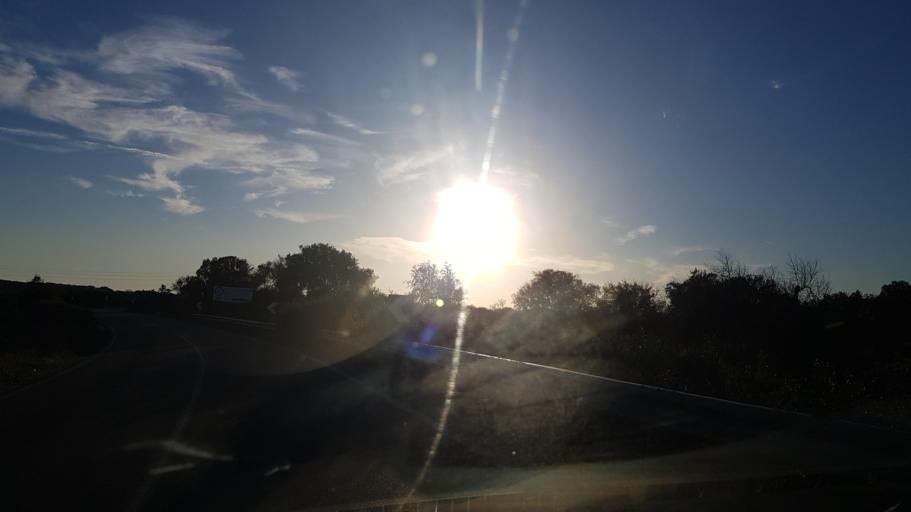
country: IT
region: Apulia
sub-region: Provincia di Lecce
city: Giorgilorio
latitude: 40.4185
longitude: 18.2077
